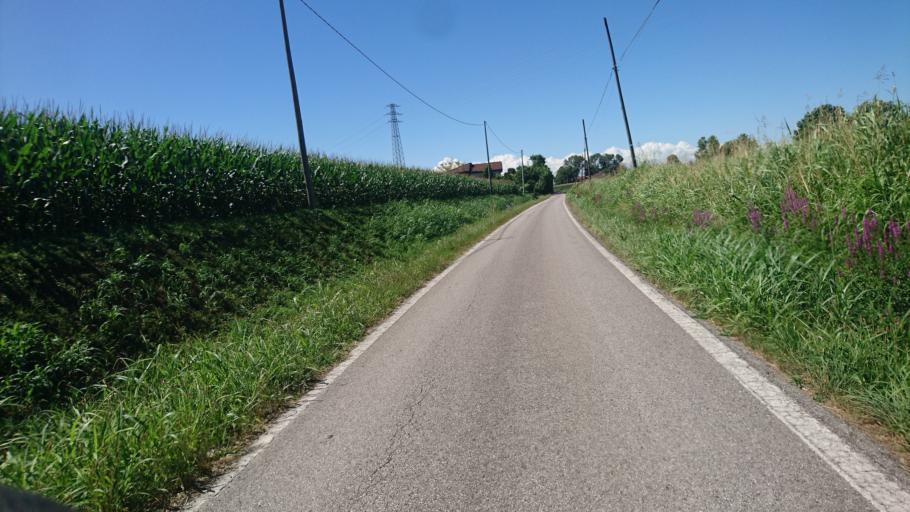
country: IT
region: Veneto
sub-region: Provincia di Padova
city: Campagnola
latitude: 45.2724
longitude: 12.0188
